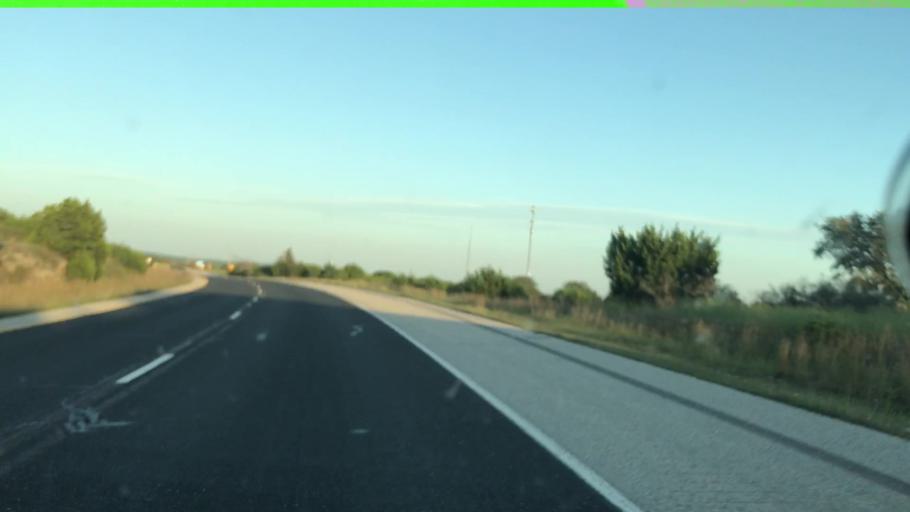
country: US
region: Texas
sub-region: Kerr County
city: Kerrville
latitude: 30.0534
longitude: -99.0335
